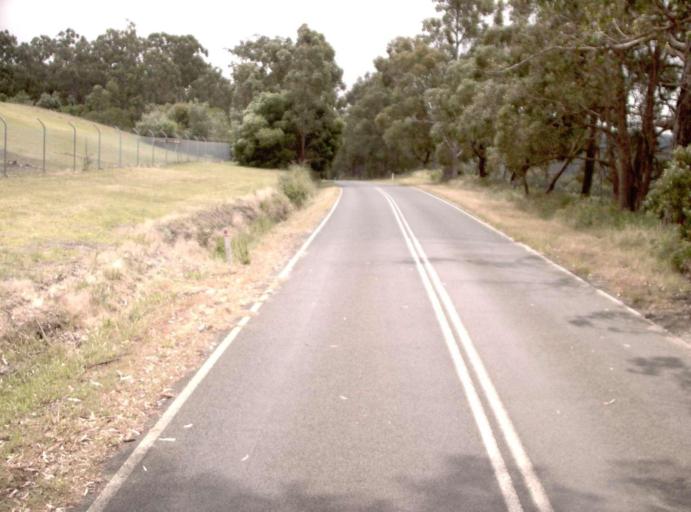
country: AU
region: Victoria
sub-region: Latrobe
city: Traralgon
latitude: -38.5003
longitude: 146.6469
